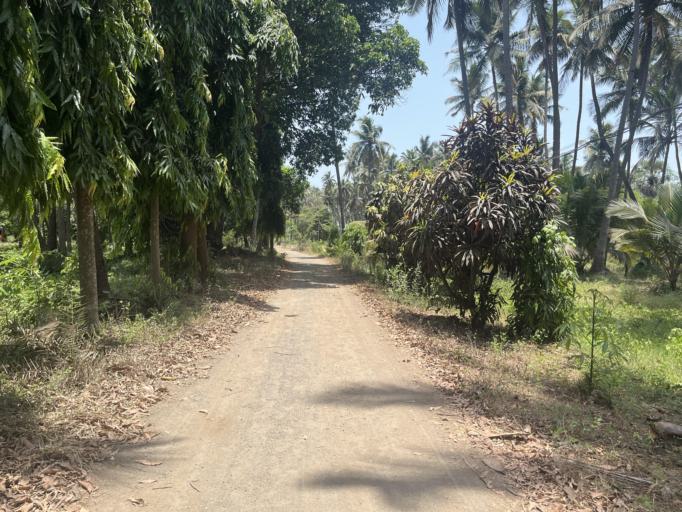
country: IN
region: Daman and Diu
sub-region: Daman District
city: Daman
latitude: 20.3517
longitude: 72.8105
